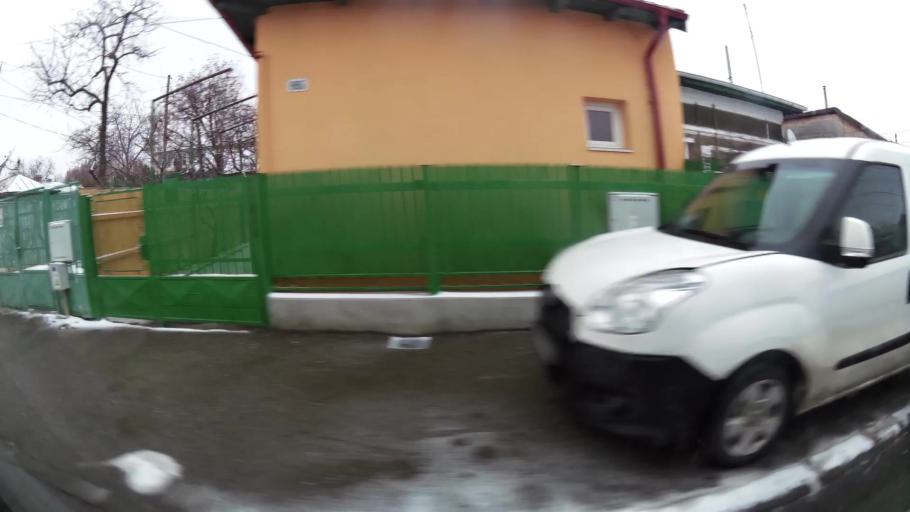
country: RO
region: Prahova
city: Ploiesti
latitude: 44.9326
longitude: 26.0474
